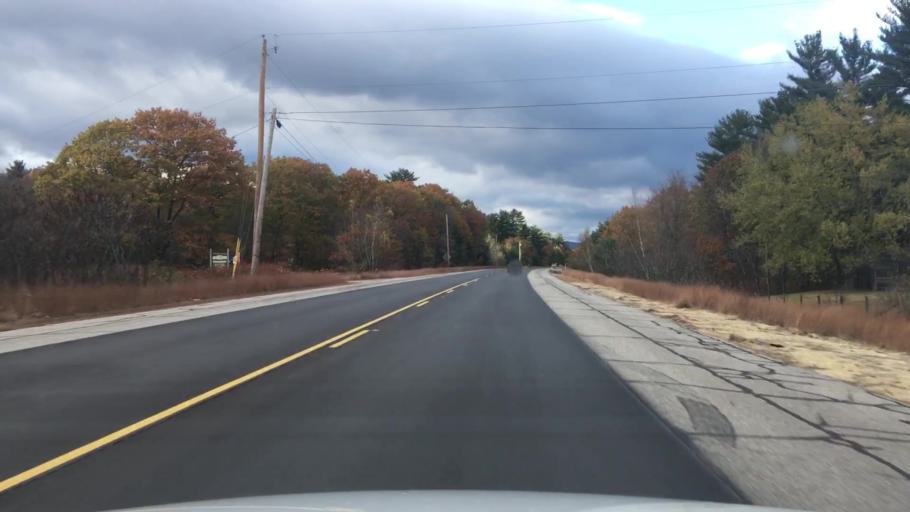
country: US
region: Maine
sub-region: Androscoggin County
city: Livermore
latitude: 44.3475
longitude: -70.2570
